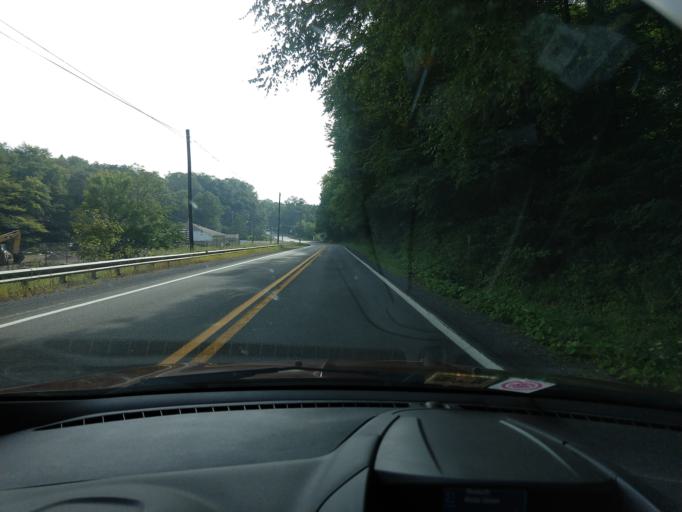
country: US
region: West Virginia
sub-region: Greenbrier County
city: Rainelle
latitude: 38.0538
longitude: -80.7161
